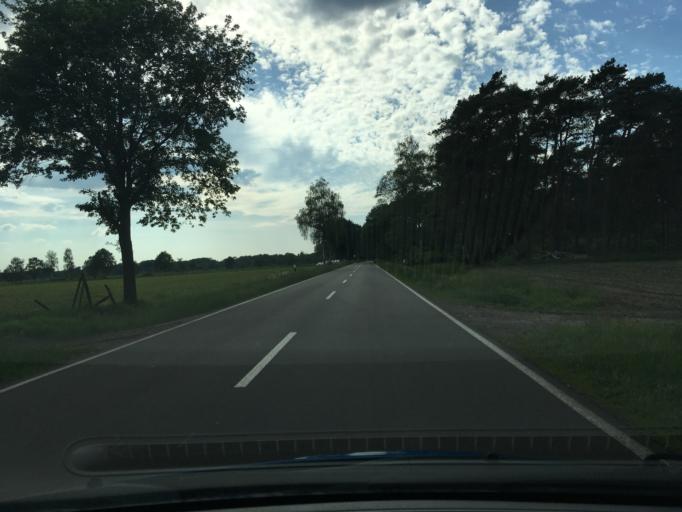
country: DE
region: Lower Saxony
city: Wistedt
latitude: 53.2745
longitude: 9.6331
